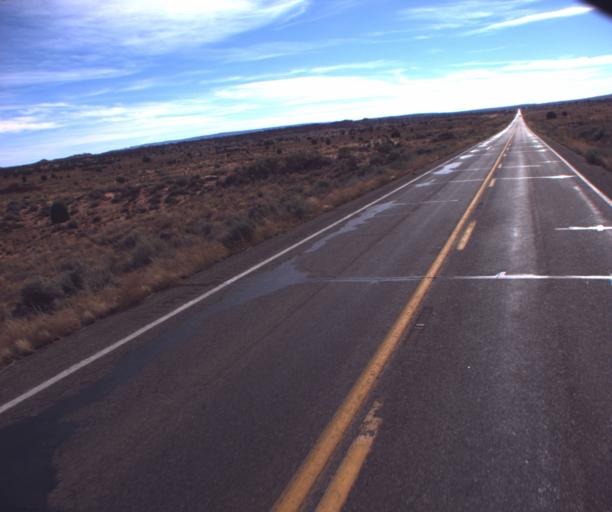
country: US
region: Arizona
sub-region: Coconino County
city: Kaibito
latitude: 36.6147
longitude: -111.1904
